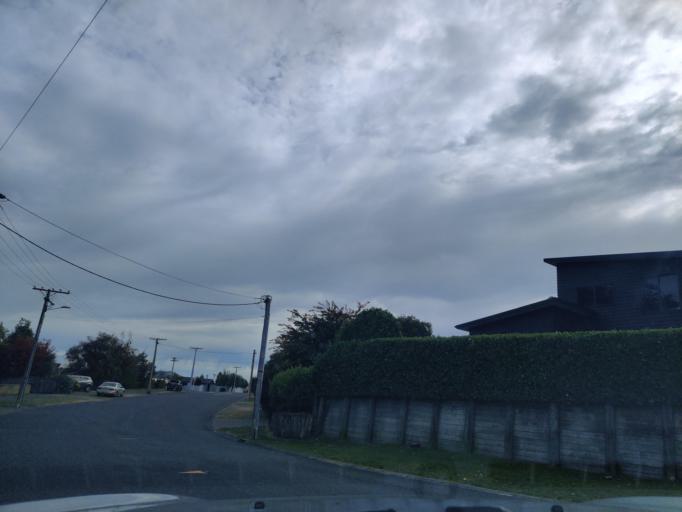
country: NZ
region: Waikato
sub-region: Taupo District
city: Taupo
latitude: -38.7095
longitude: 176.0944
